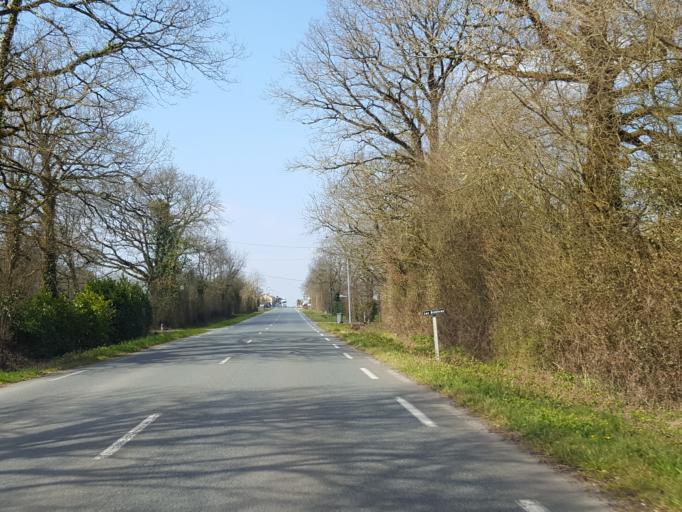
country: FR
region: Pays de la Loire
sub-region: Departement de la Vendee
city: La Chaize-le-Vicomte
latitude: 46.6676
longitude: -1.2815
